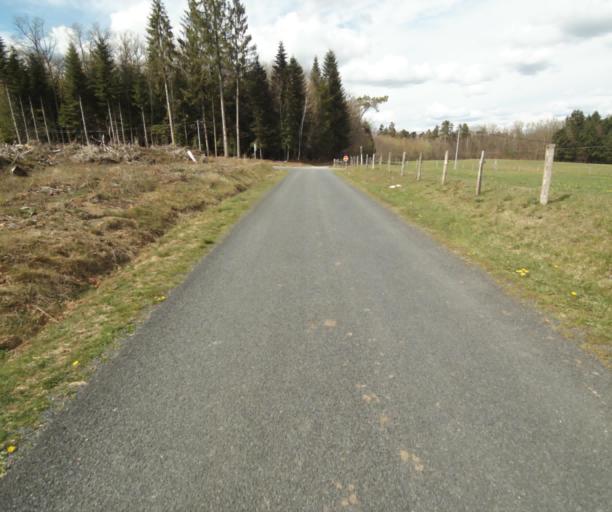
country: FR
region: Limousin
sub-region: Departement de la Correze
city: Argentat
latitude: 45.2054
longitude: 1.9034
